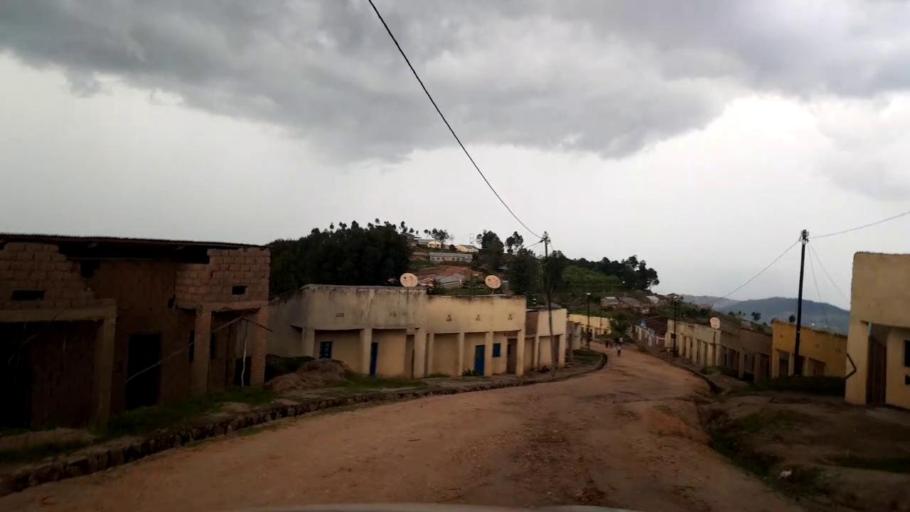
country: RW
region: Southern Province
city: Gitarama
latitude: -1.8709
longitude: 29.5901
